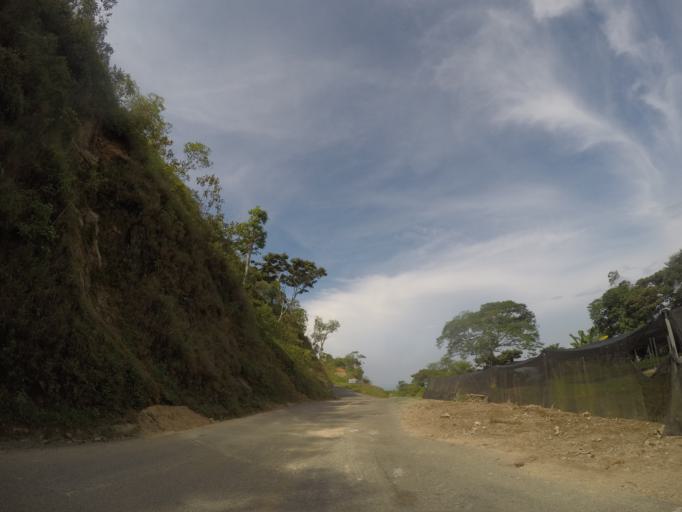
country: MX
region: Oaxaca
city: Pluma Hidalgo
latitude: 15.9317
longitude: -96.4234
